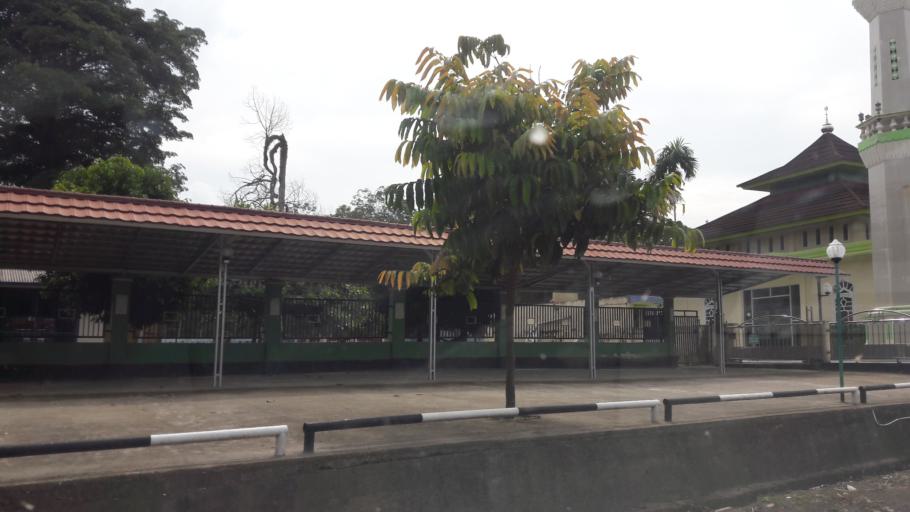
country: ID
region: South Sumatra
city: Gunungmenang
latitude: -3.1519
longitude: 104.1178
